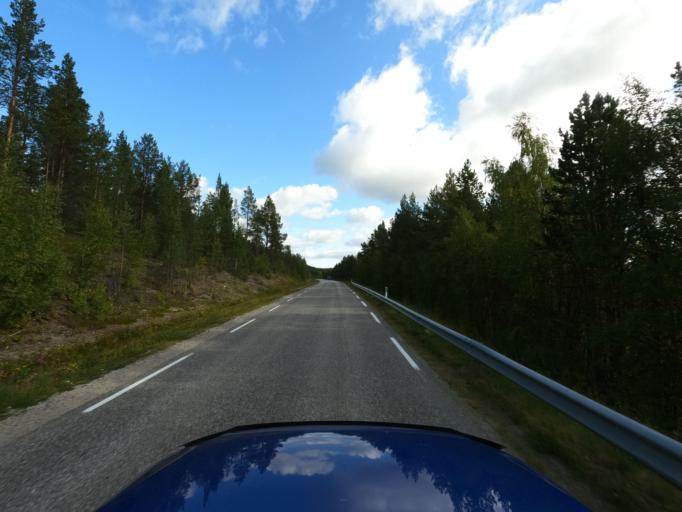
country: NO
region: Finnmark Fylke
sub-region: Karasjok
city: Karasjohka
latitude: 69.4552
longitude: 25.3948
